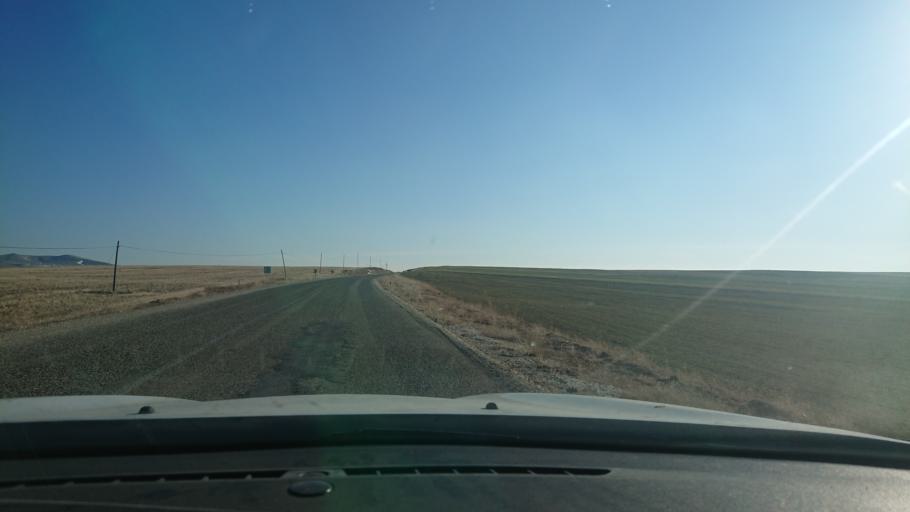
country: TR
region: Aksaray
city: Agacoren
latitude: 38.7800
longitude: 33.8715
